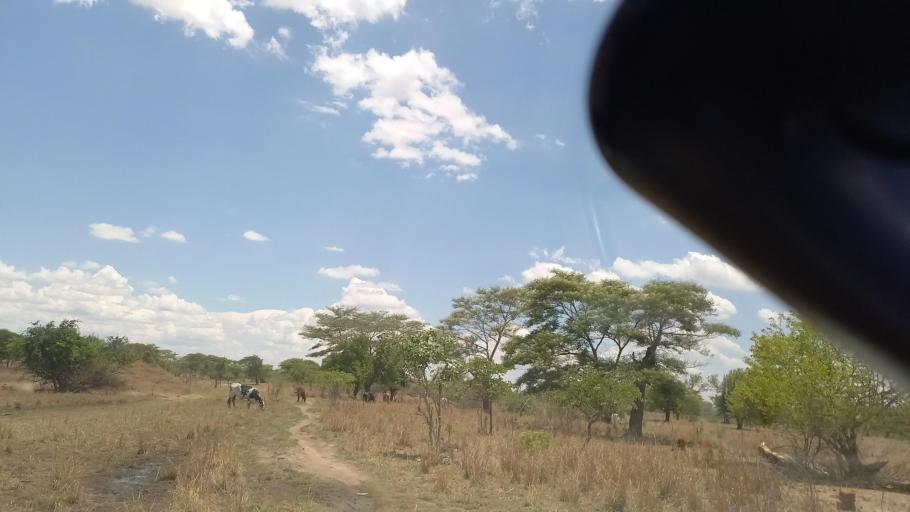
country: ZM
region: Southern
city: Mazabuka
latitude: -16.1224
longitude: 27.7774
